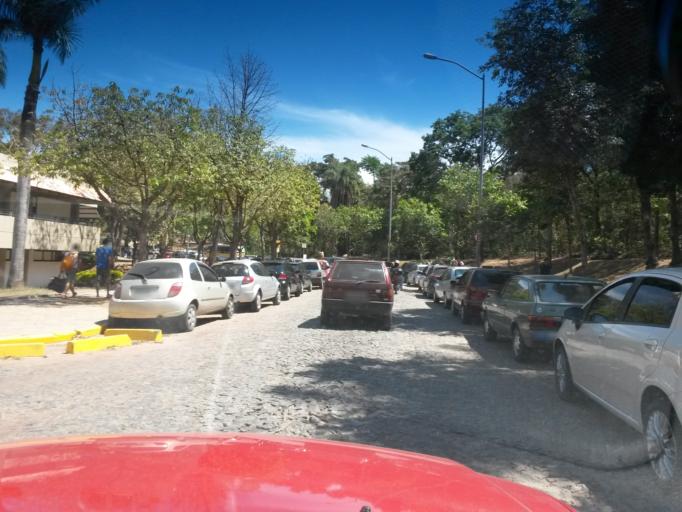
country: BR
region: Minas Gerais
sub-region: Belo Horizonte
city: Belo Horizonte
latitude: -19.8674
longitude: -43.9674
